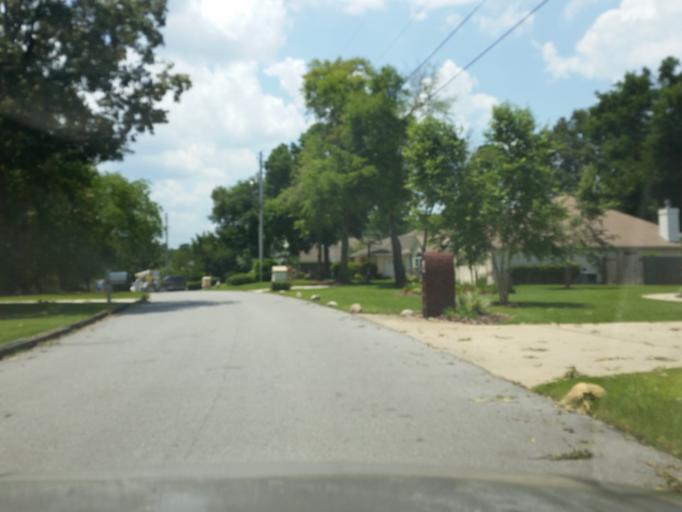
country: US
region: Florida
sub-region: Escambia County
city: Ferry Pass
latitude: 30.5387
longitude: -87.1961
